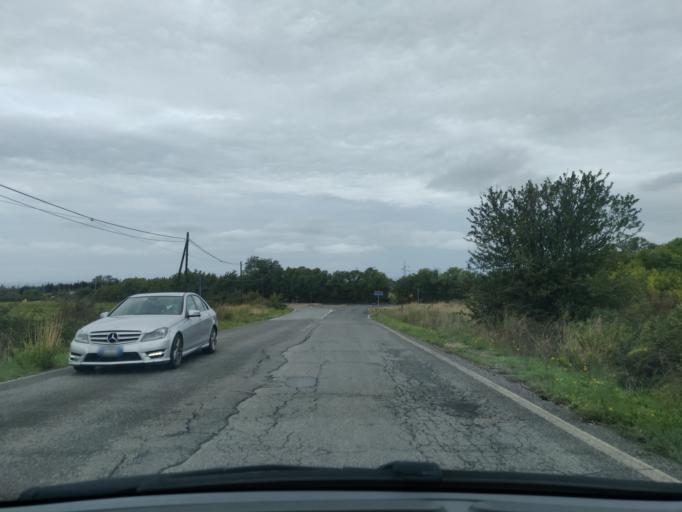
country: IT
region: Latium
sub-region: Citta metropolitana di Roma Capitale
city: Civitavecchia
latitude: 42.1077
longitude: 11.8342
